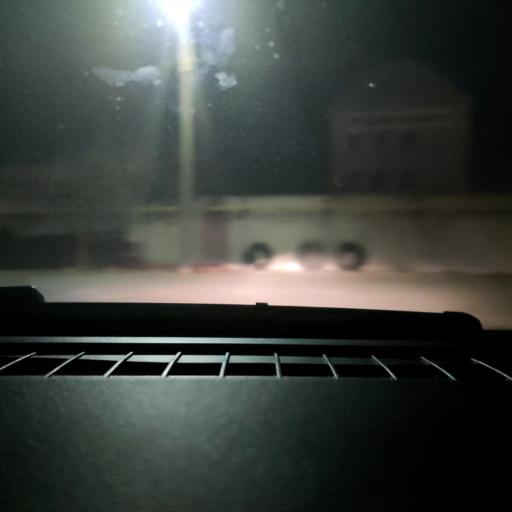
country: RU
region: Voronezj
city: Somovo
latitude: 51.6759
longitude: 39.2952
